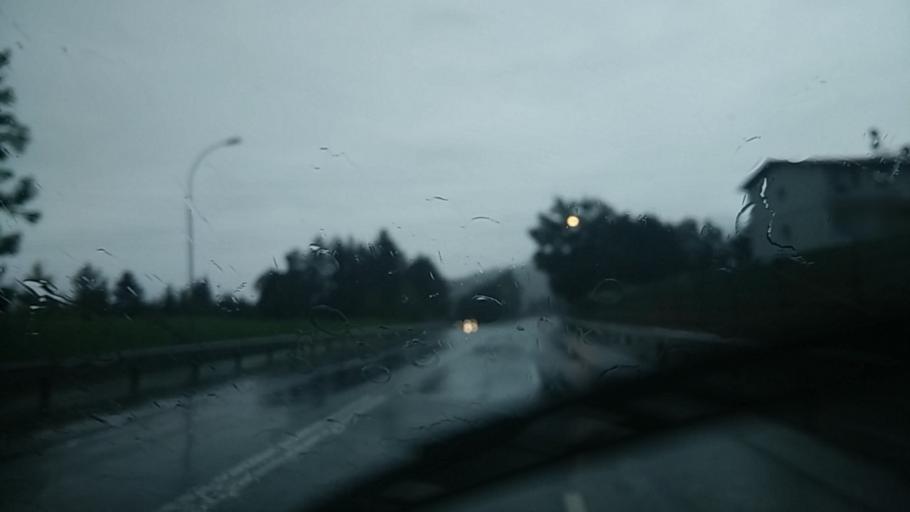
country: AT
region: Carinthia
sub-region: Villach Stadt
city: Villach
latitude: 46.6258
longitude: 13.8878
